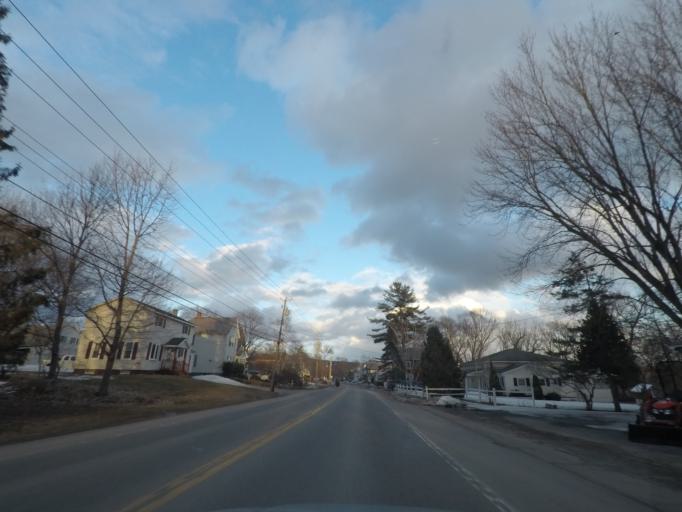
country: US
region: New York
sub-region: Montgomery County
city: Saint Johnsville
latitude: 42.9982
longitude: -74.6901
